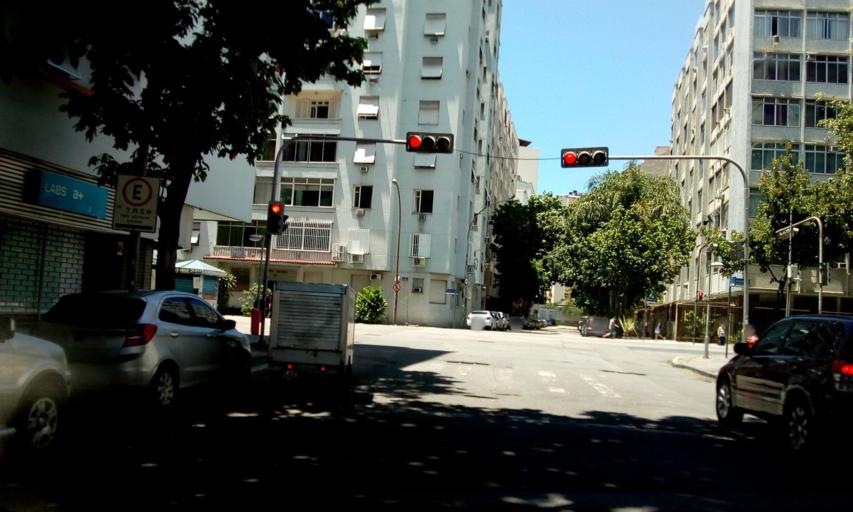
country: BR
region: Rio de Janeiro
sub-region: Rio De Janeiro
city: Rio de Janeiro
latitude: -22.9325
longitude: -43.1790
